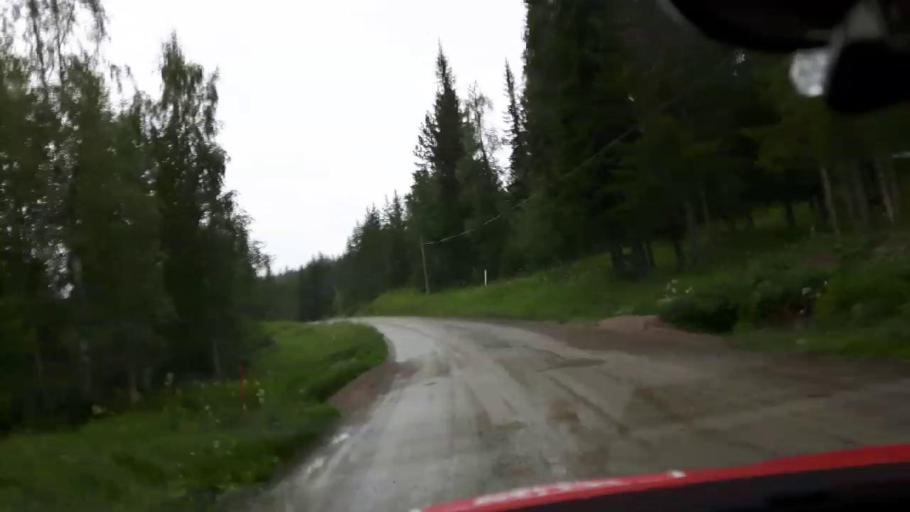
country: SE
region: Jaemtland
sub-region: OEstersunds Kommun
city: Brunflo
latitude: 62.8849
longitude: 14.8750
